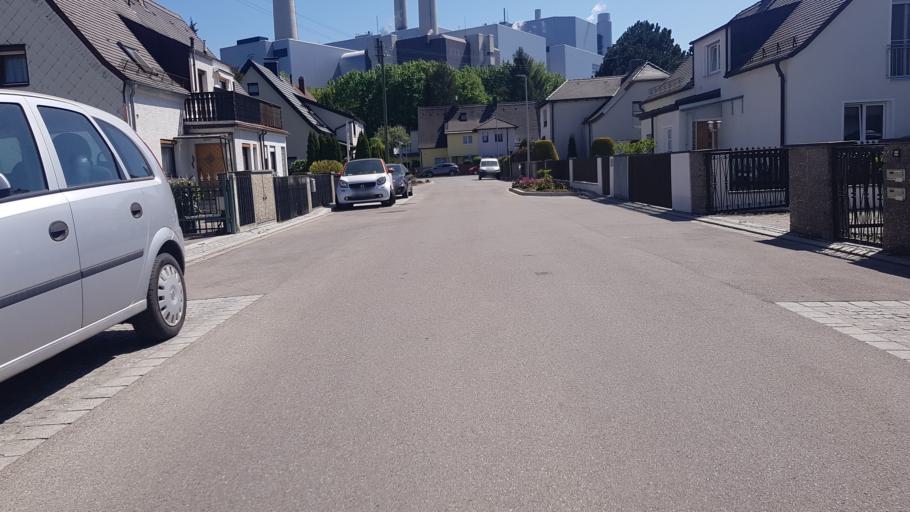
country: DE
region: Bavaria
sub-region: Upper Bavaria
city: Unterfoehring
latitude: 48.1816
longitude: 11.6351
